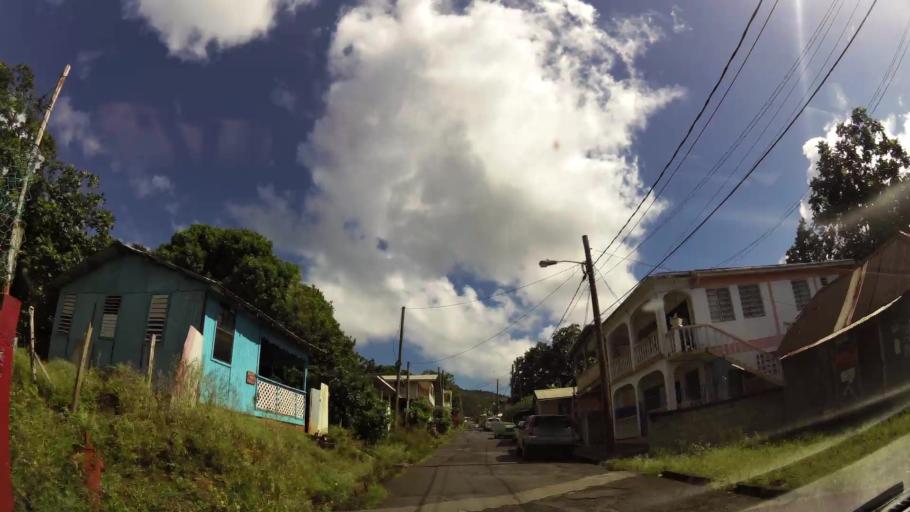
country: DM
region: Saint John
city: Portsmouth
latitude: 15.5777
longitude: -61.4552
